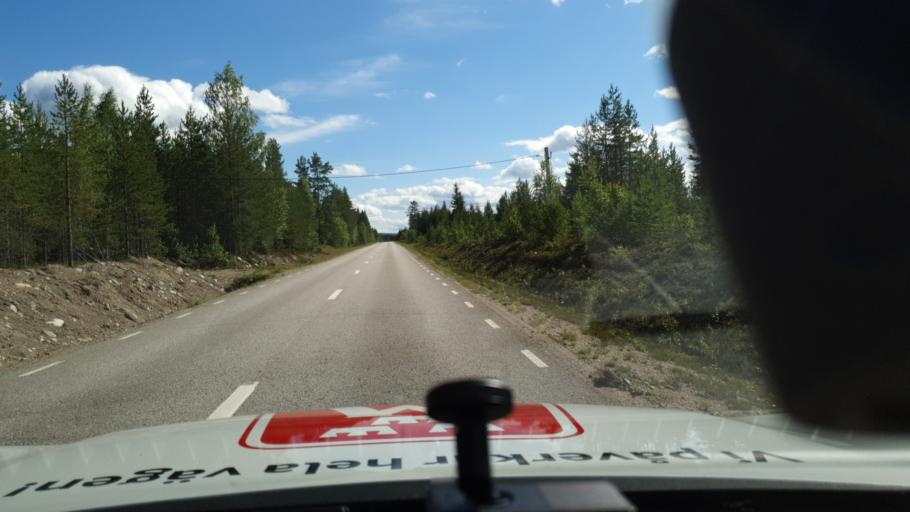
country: NO
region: Hedmark
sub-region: Trysil
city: Innbygda
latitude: 60.9829
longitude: 12.4926
